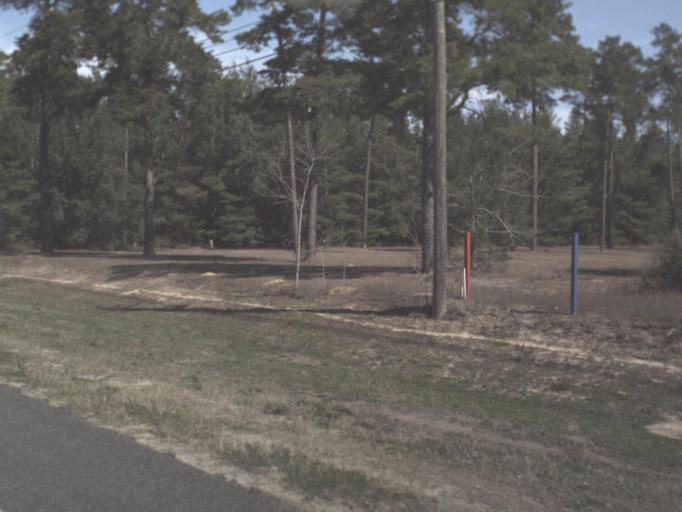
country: US
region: Florida
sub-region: Bay County
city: Lynn Haven
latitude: 30.3994
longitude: -85.6894
